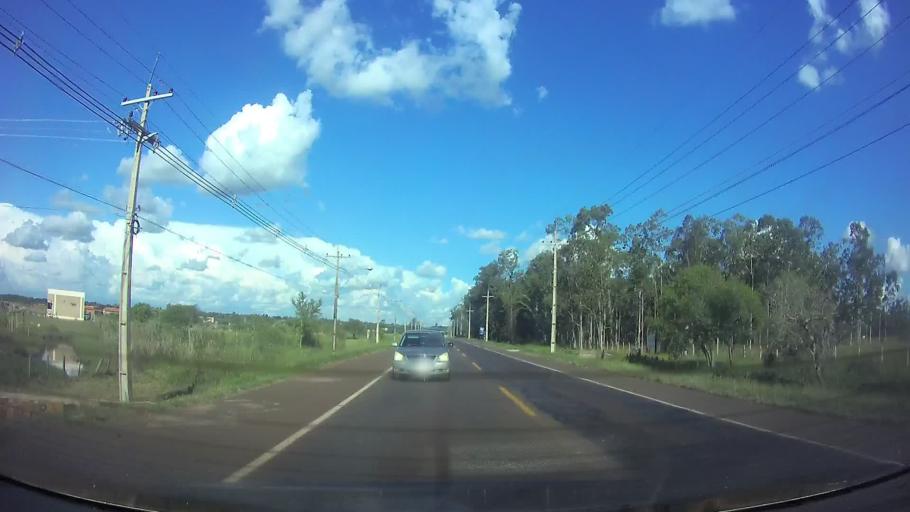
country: PY
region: Cordillera
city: Eusebio Ayala
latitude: -25.3810
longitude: -56.9826
